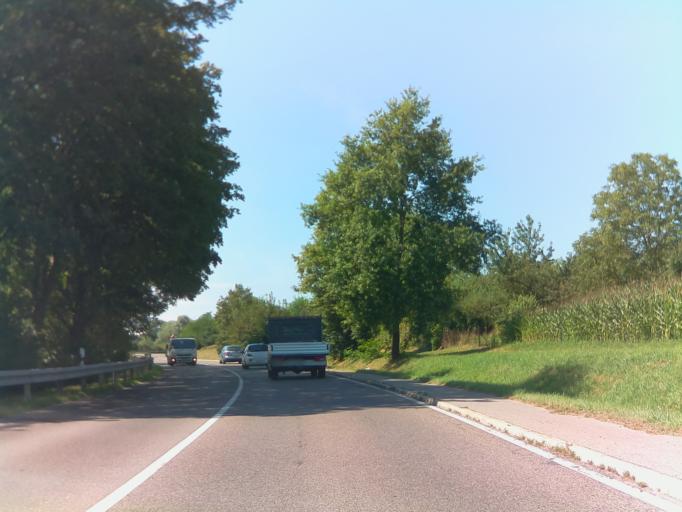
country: DE
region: Baden-Wuerttemberg
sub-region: Regierungsbezirk Stuttgart
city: Leonberg
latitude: 48.8014
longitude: 8.9858
